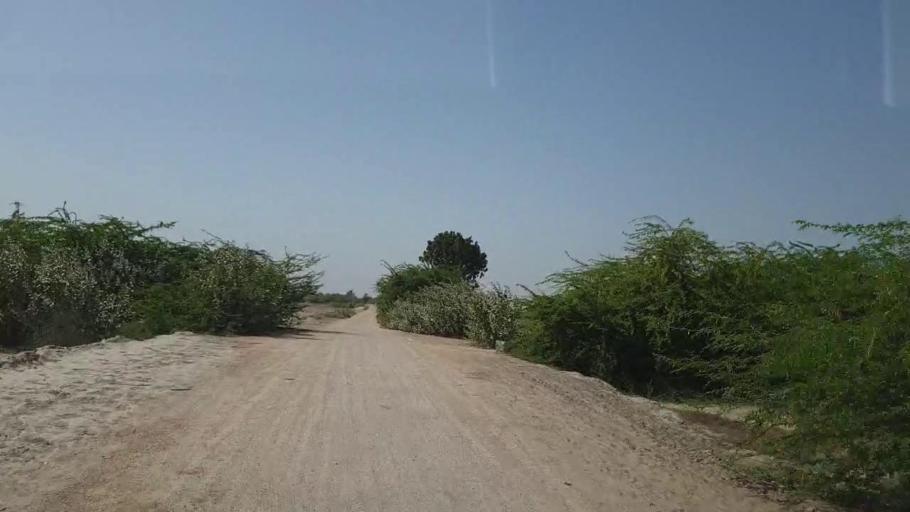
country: PK
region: Sindh
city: Naukot
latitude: 24.9568
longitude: 69.5162
